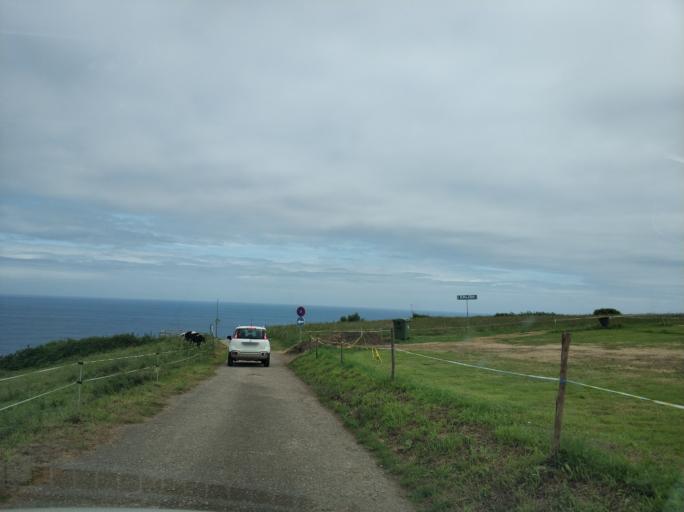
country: ES
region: Asturias
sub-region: Province of Asturias
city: Cudillero
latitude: 43.5639
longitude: -6.2980
